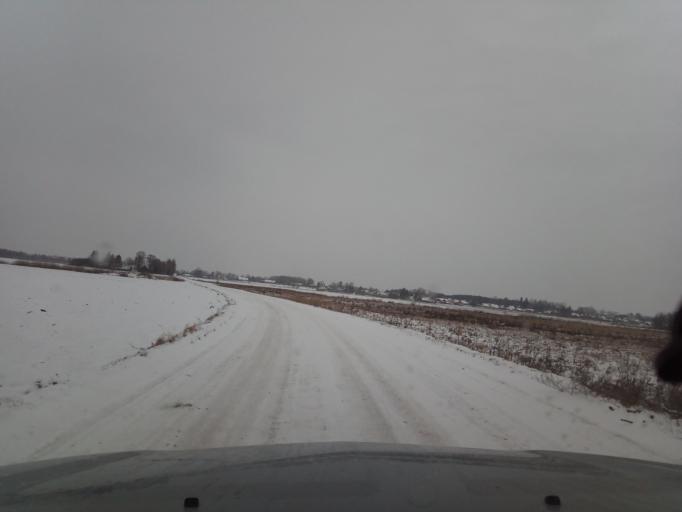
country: LT
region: Panevezys
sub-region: Panevezys City
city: Panevezys
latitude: 55.6174
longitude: 24.3781
